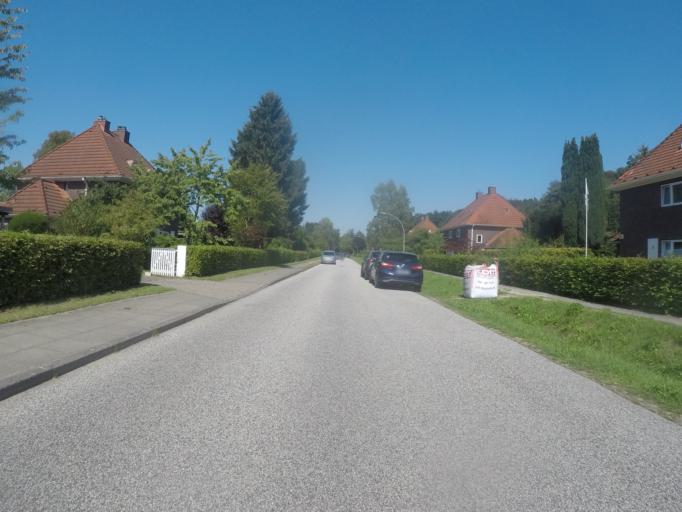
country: DE
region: Hamburg
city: Farmsen-Berne
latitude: 53.6310
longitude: 10.1253
